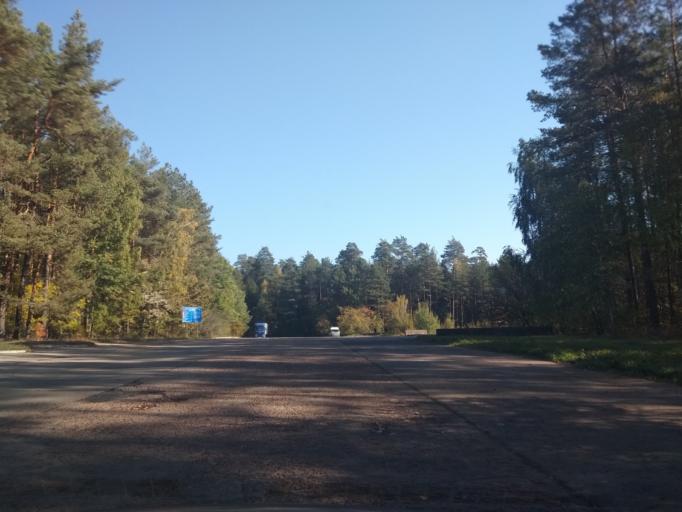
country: BY
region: Brest
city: Ivatsevichy
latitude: 52.8565
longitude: 25.6481
